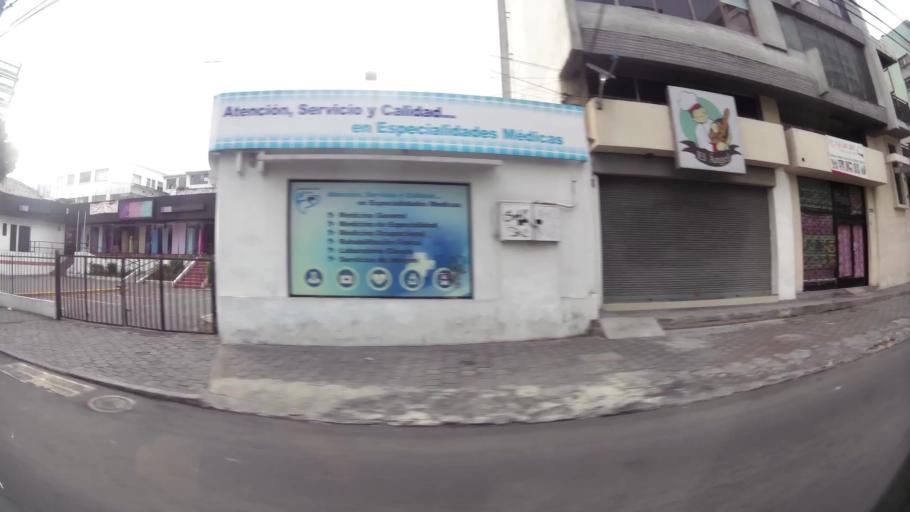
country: EC
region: Pichincha
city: Quito
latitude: -0.1992
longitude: -78.4850
